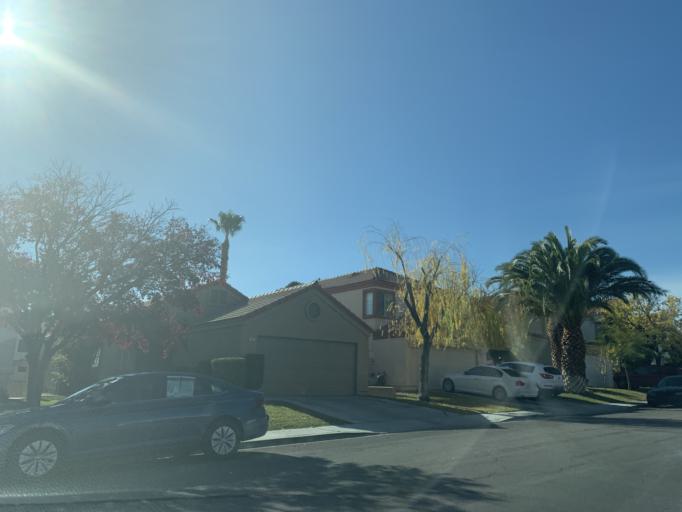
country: US
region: Nevada
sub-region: Clark County
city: Summerlin South
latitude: 36.1329
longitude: -115.2949
